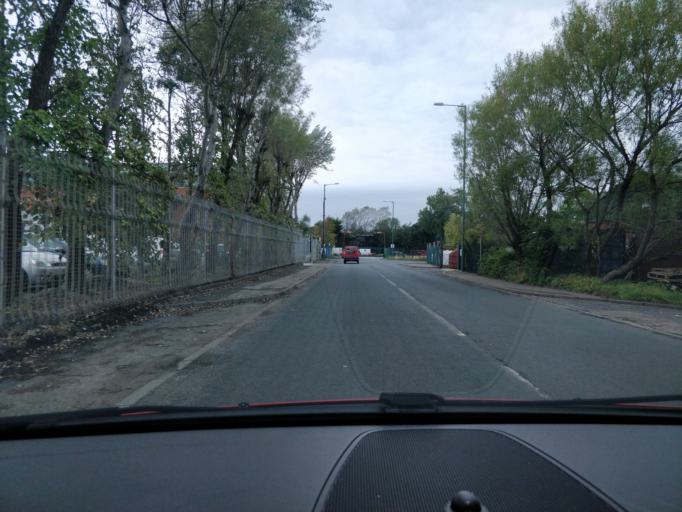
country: GB
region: England
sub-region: Lancashire
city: Ormskirk
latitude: 53.6021
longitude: -2.8660
